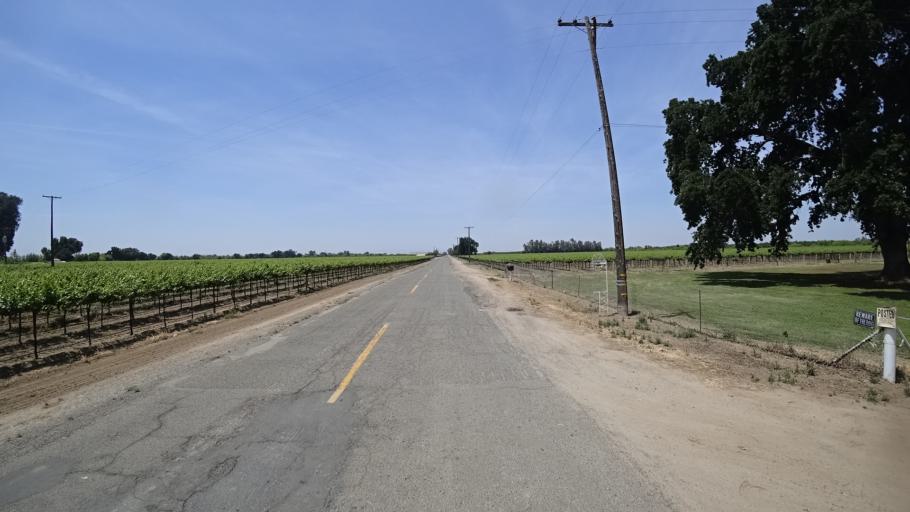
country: US
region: California
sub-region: Fresno County
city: Riverdale
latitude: 36.3875
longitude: -119.8547
